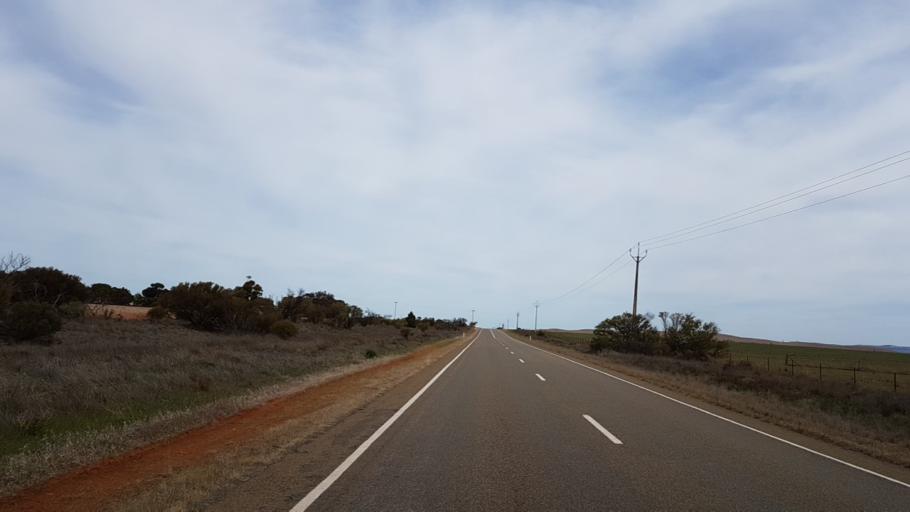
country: AU
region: South Australia
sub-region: Peterborough
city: Peterborough
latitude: -32.9991
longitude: 138.7798
